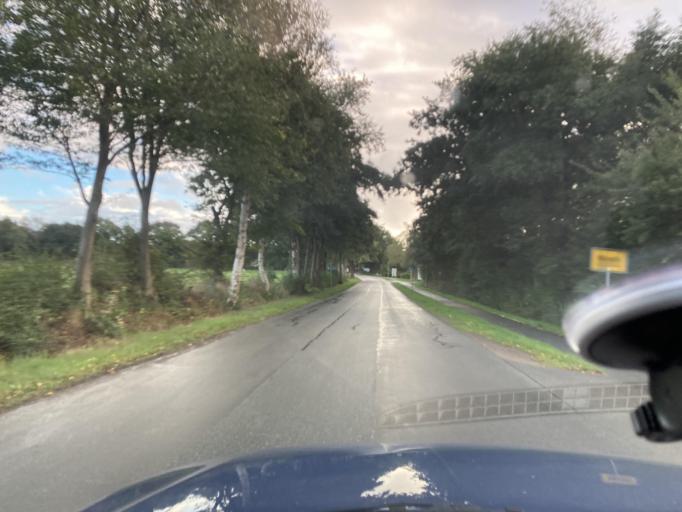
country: DE
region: Schleswig-Holstein
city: Heide
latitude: 54.2096
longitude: 9.0945
